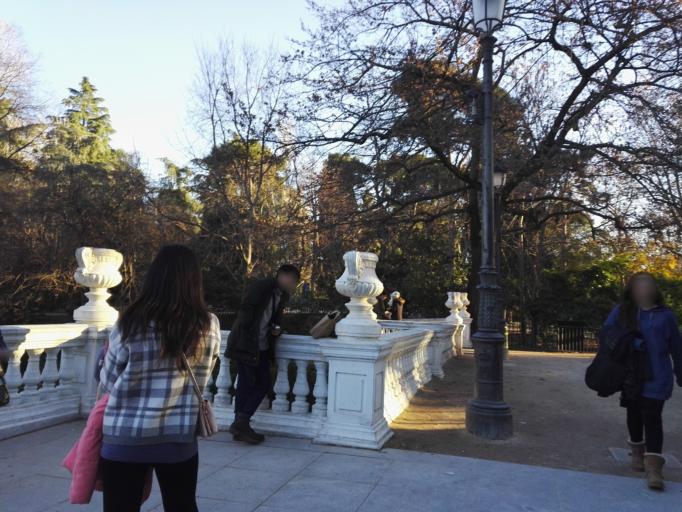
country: ES
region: Madrid
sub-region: Provincia de Madrid
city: Retiro
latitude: 40.4135
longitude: -3.6817
